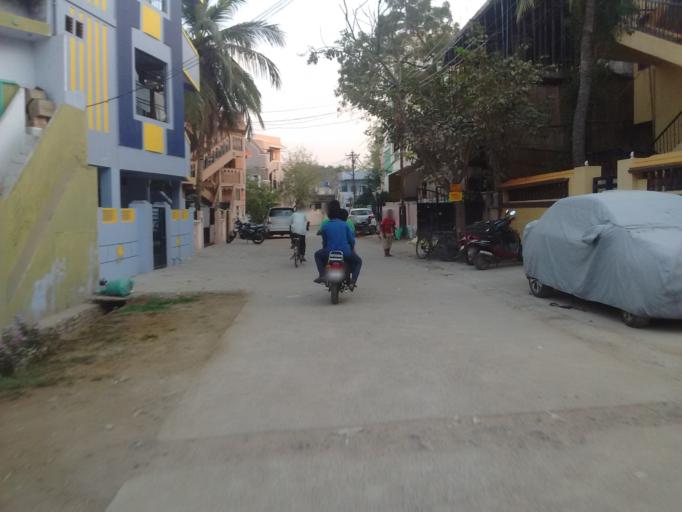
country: IN
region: Telangana
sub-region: Mahbubnagar
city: Alampur
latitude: 15.8107
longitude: 78.0426
